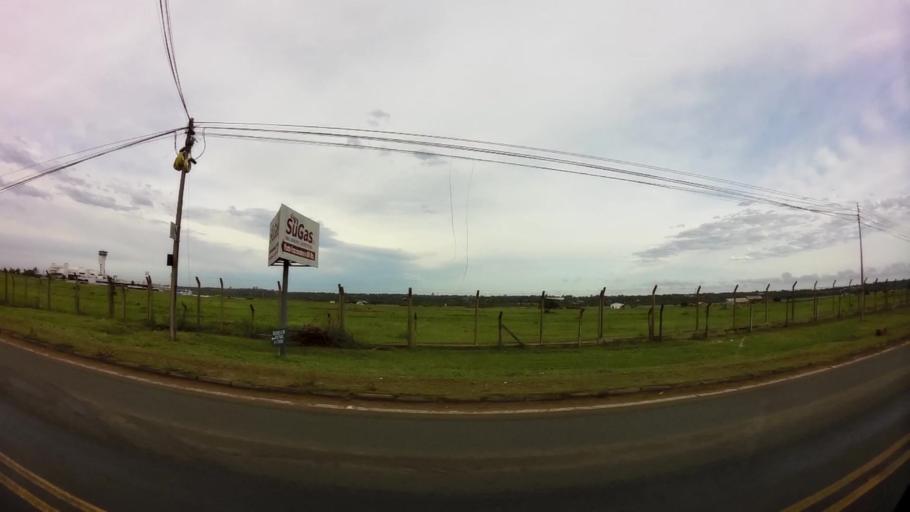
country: PY
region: Central
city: Limpio
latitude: -25.2375
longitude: -57.5100
